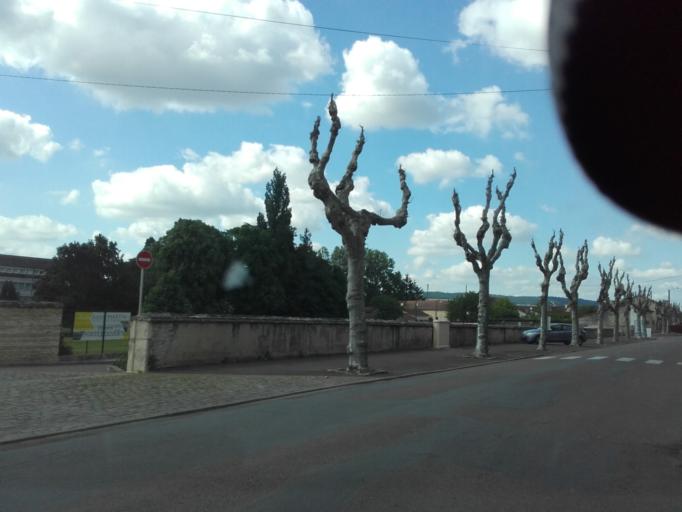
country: FR
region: Bourgogne
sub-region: Departement de Saone-et-Loire
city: Chagny
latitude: 46.9127
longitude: 4.7533
